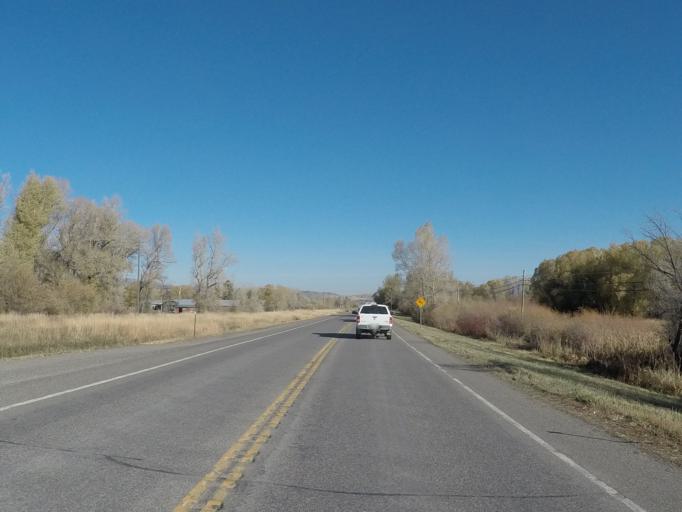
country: US
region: Montana
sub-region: Park County
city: Livingston
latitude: 45.6200
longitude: -110.5789
